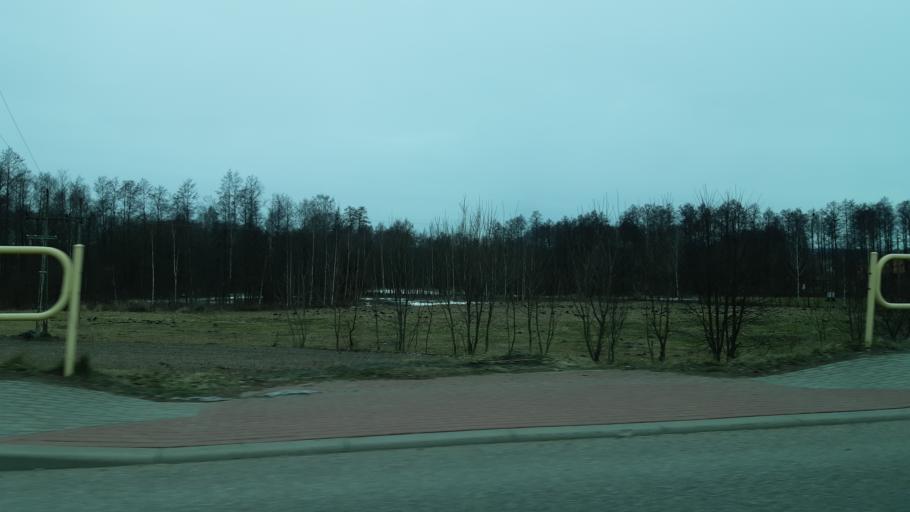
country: PL
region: Podlasie
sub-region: Suwalki
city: Suwalki
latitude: 54.3212
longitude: 22.9680
